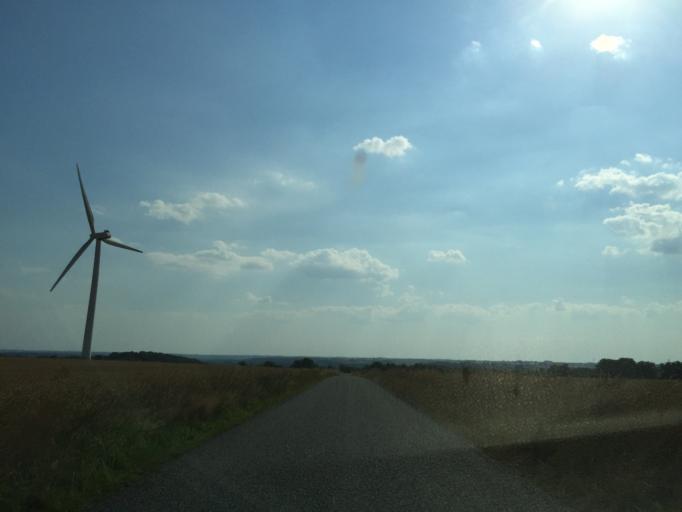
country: DK
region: Central Jutland
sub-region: Viborg Kommune
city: Bjerringbro
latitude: 56.2573
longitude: 9.6877
